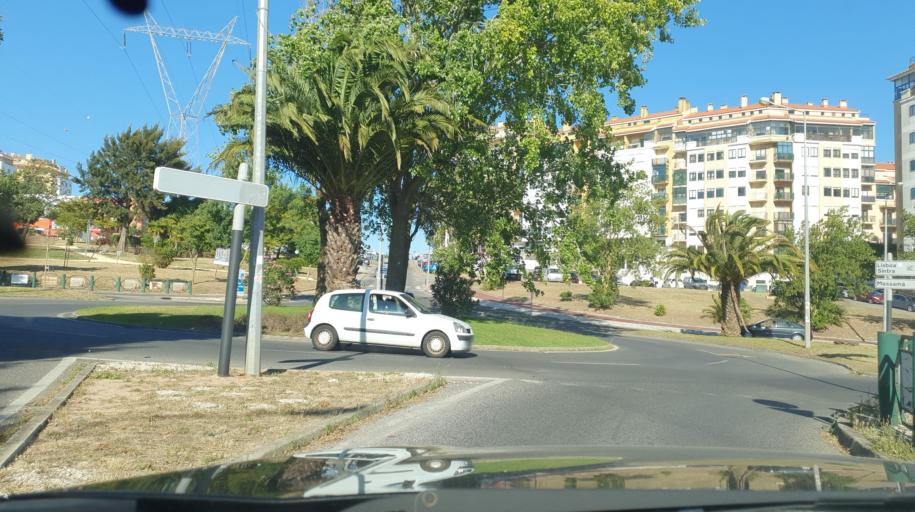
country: PT
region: Lisbon
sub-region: Sintra
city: Cacem
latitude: 38.7616
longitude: -9.2788
